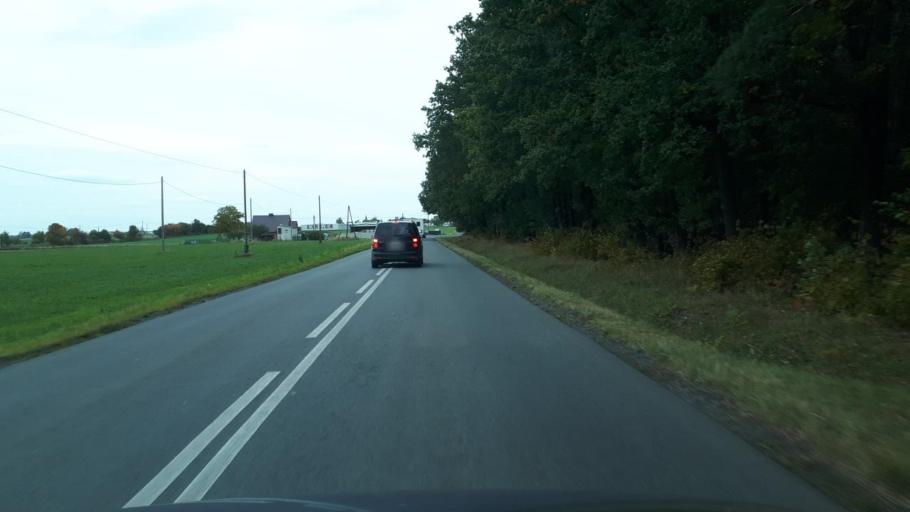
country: PL
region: Opole Voivodeship
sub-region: Powiat oleski
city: Dobrodzien
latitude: 50.7086
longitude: 18.4457
